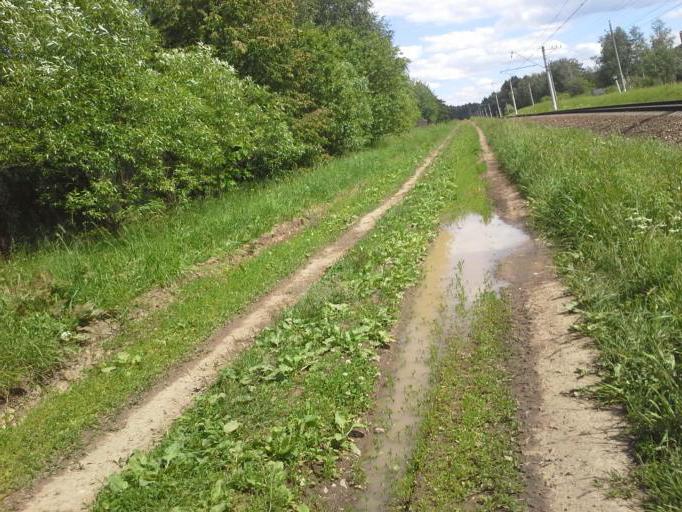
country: RU
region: Moscow
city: Tolstopal'tsevo
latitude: 55.6226
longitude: 37.2241
